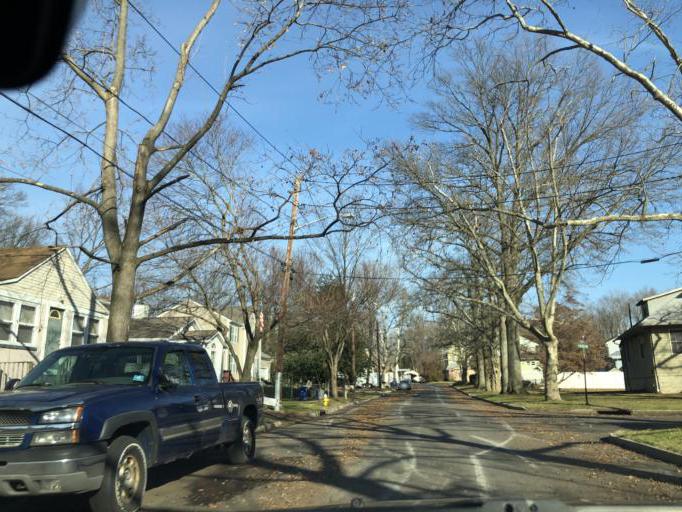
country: US
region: New Jersey
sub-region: Burlington County
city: Maple Shade
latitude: 39.9627
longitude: -74.9848
